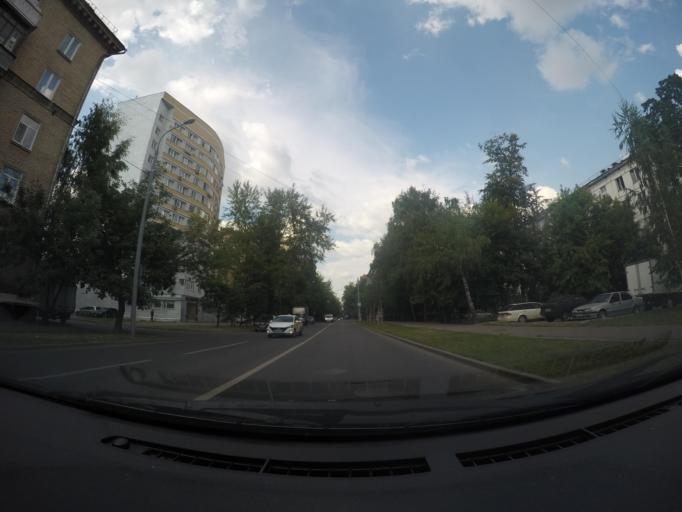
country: RU
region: Moscow
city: Otradnoye
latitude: 55.8536
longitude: 37.6076
